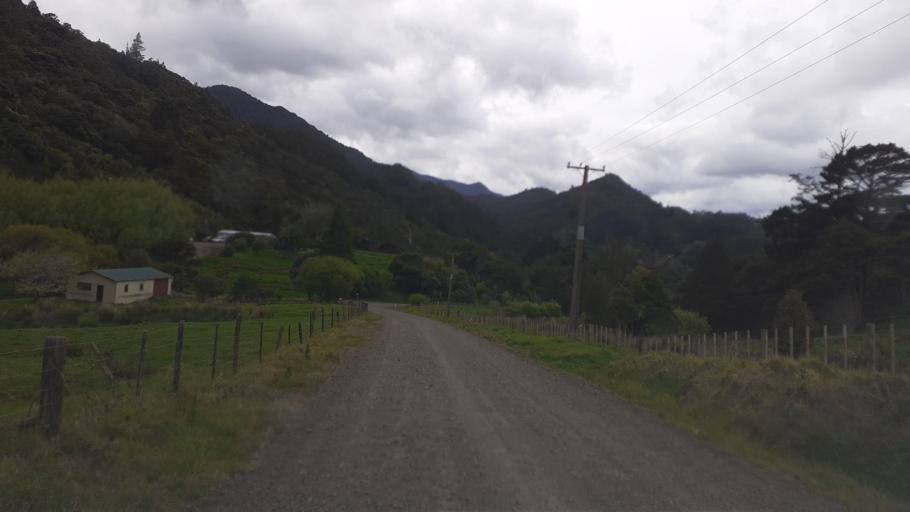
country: NZ
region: Northland
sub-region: Far North District
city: Kaitaia
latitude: -35.5313
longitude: 173.4313
